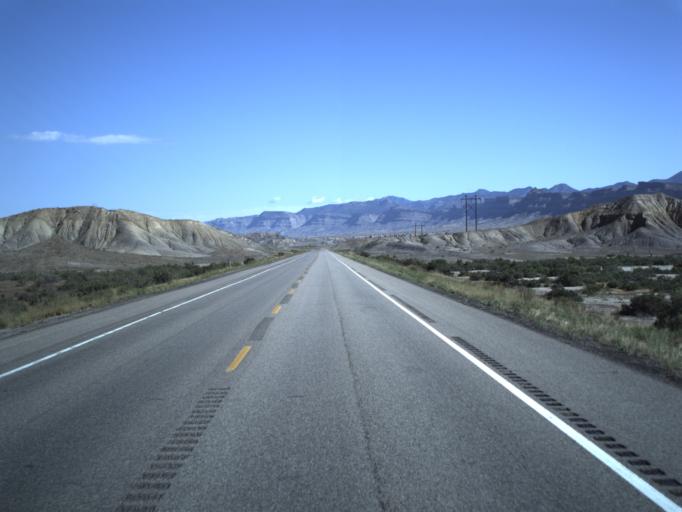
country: US
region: Utah
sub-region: Carbon County
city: East Carbon City
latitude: 39.2454
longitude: -110.3389
